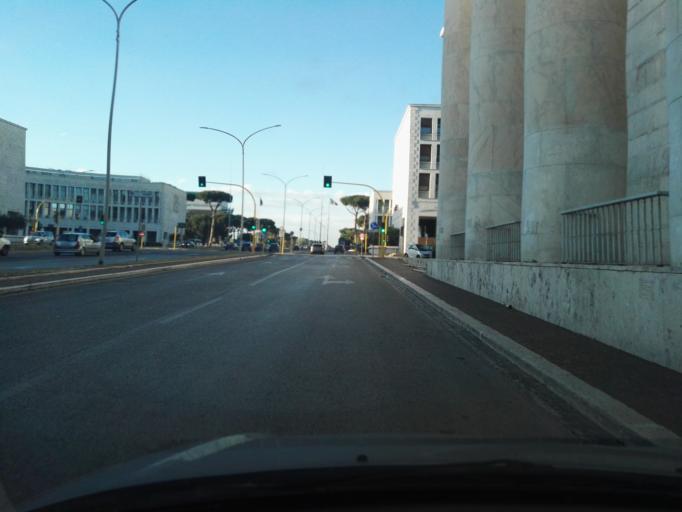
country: IT
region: Latium
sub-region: Citta metropolitana di Roma Capitale
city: Selcetta
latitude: 41.8342
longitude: 12.4715
